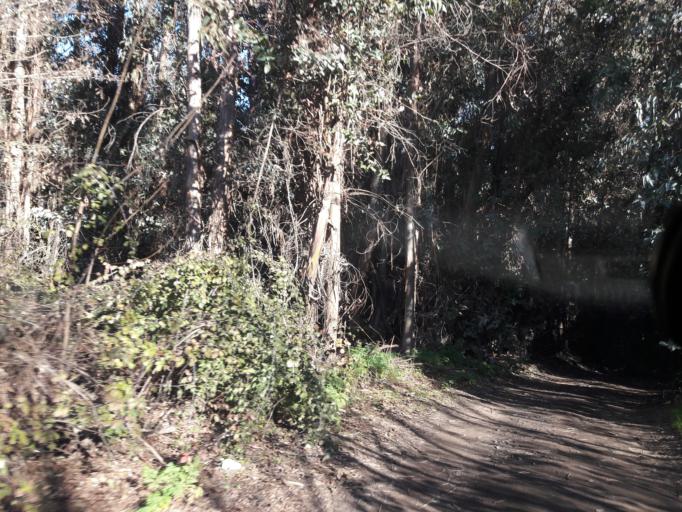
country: CL
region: Biobio
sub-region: Provincia de Biobio
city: Cabrero
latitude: -37.0253
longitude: -72.1912
